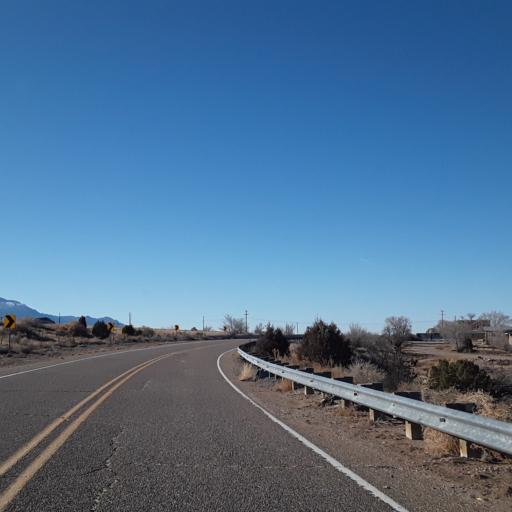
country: US
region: New Mexico
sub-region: Sandoval County
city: Santo Domingo Pueblo
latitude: 35.4592
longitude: -106.3340
